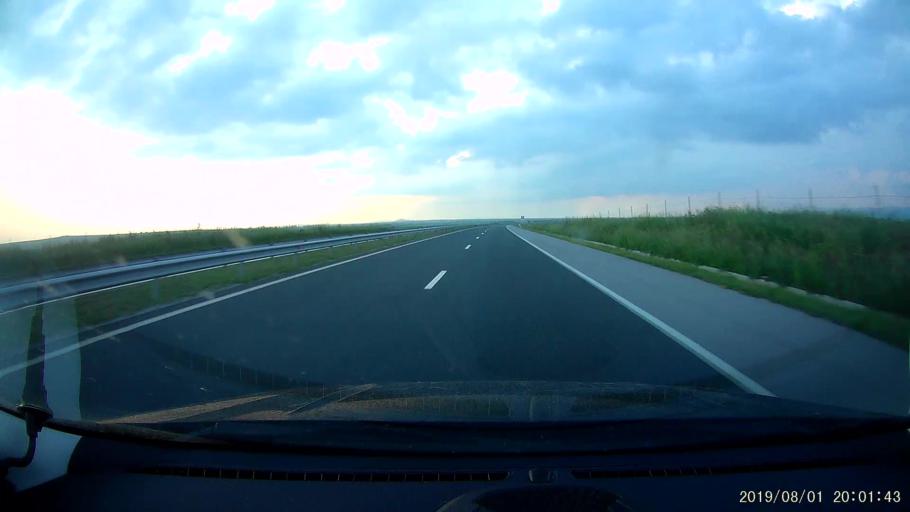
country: BG
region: Yambol
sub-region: Obshtina Straldzha
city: Straldzha
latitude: 42.5563
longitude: 26.6556
